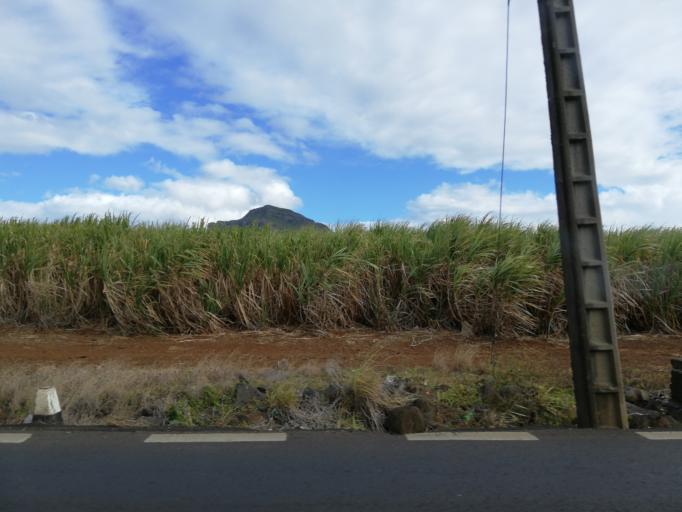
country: MU
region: Black River
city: Gros Cailloux
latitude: -20.2308
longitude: 57.4500
